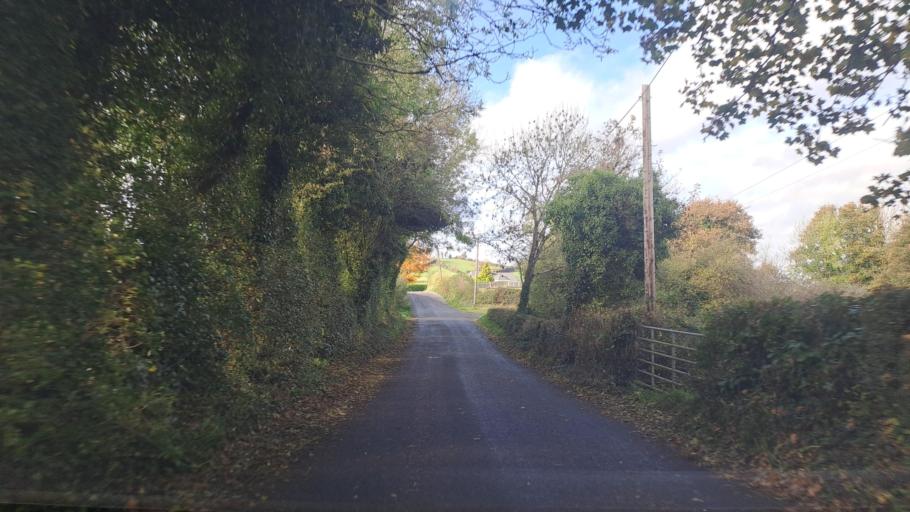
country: IE
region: Ulster
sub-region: An Cabhan
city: Cootehill
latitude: 54.0340
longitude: -7.0087
